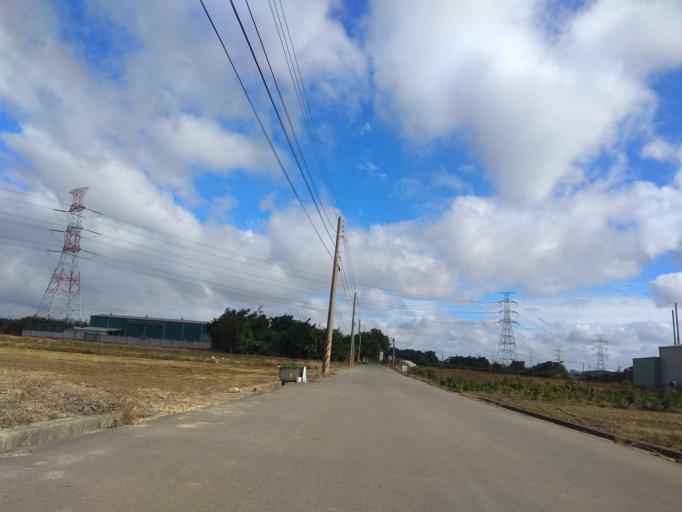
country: TW
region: Taiwan
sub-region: Hsinchu
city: Zhubei
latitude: 24.9746
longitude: 121.0711
